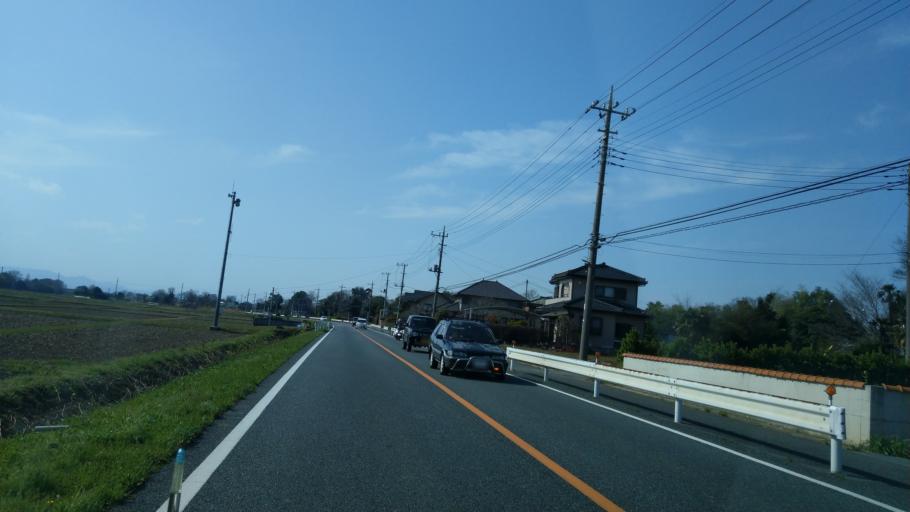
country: JP
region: Saitama
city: Okegawa
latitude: 35.9586
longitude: 139.5250
